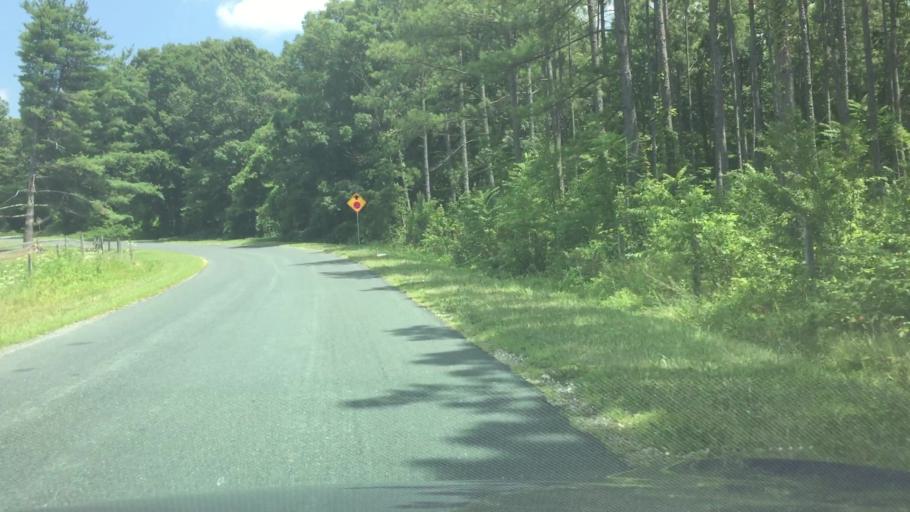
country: US
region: Virginia
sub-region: Appomattox County
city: Appomattox
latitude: 37.3205
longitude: -78.8516
